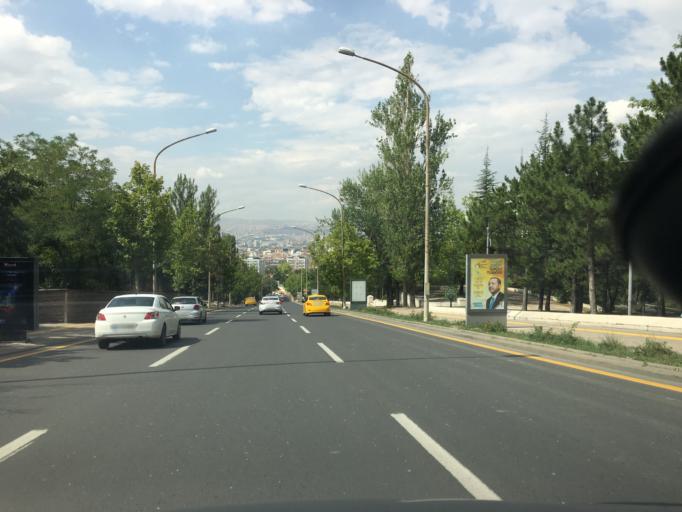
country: TR
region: Ankara
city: Cankaya
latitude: 39.8937
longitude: 32.8623
